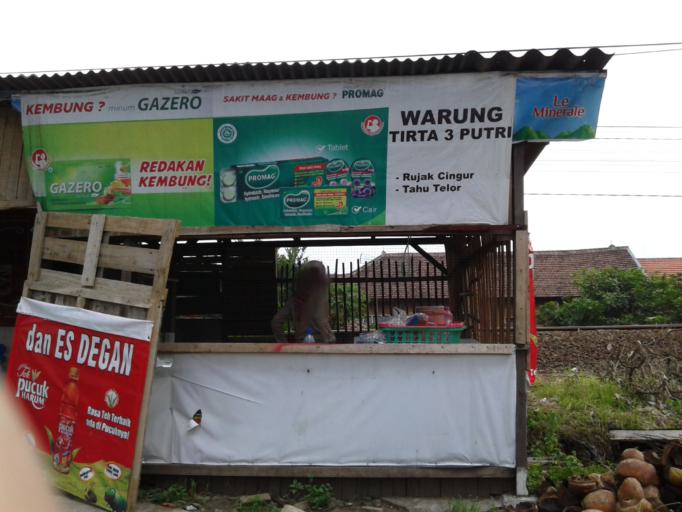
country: ID
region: East Java
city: Lawang
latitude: -7.8397
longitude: 112.6980
